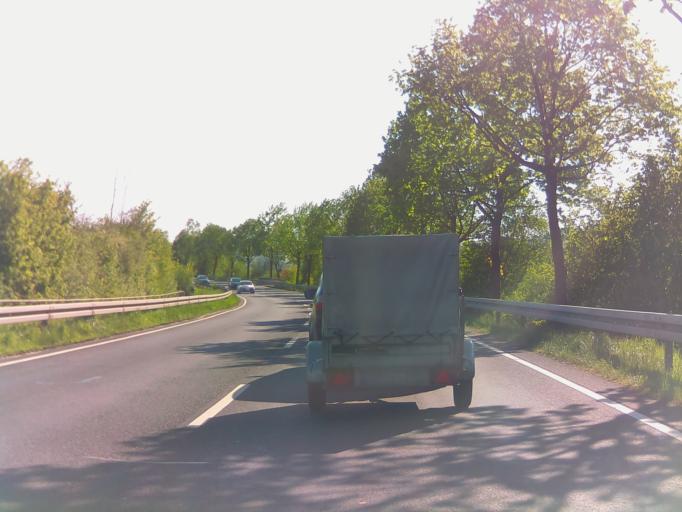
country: DE
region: Hesse
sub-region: Regierungsbezirk Darmstadt
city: Wachtersbach
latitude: 50.2618
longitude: 9.3030
